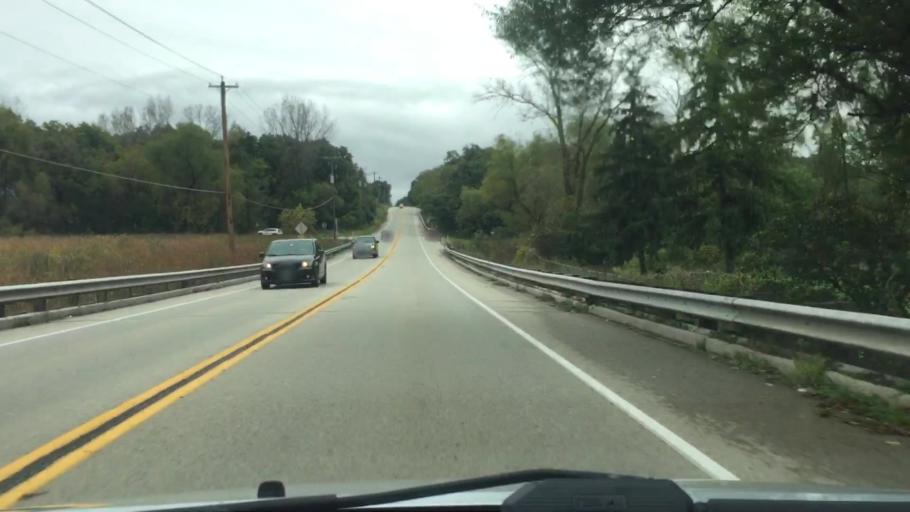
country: US
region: Wisconsin
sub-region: Walworth County
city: Elkhorn
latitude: 42.7612
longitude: -88.5538
